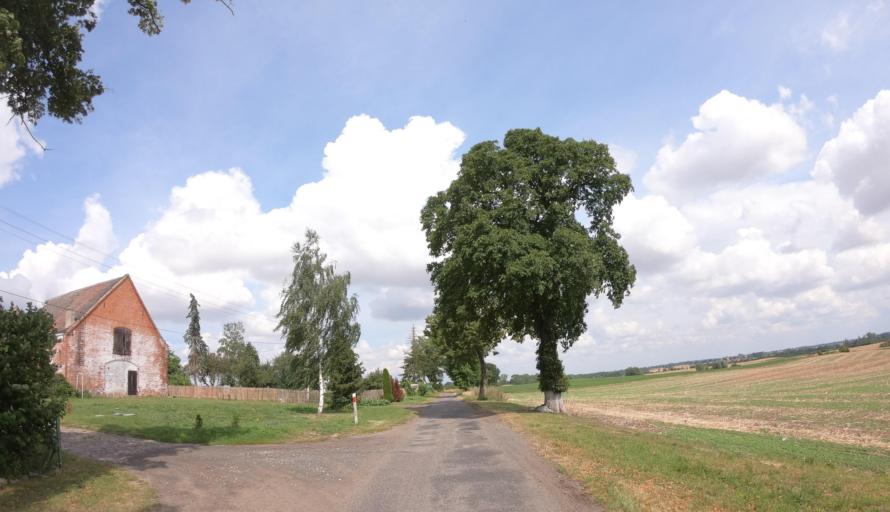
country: PL
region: West Pomeranian Voivodeship
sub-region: Powiat pyrzycki
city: Kozielice
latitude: 53.0552
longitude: 14.8926
